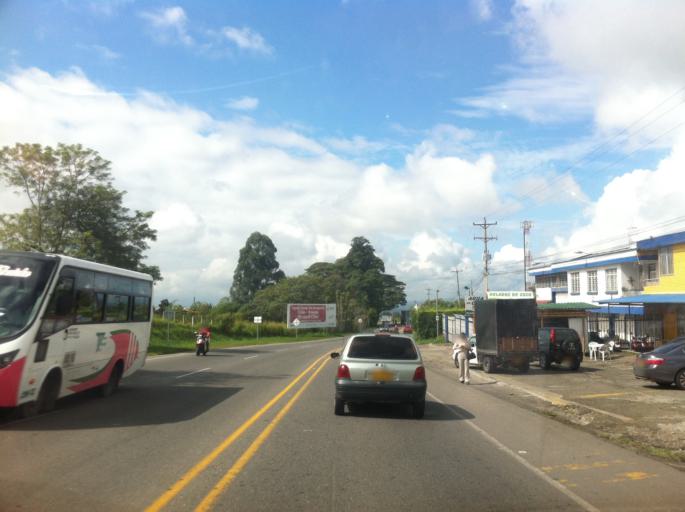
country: CO
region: Quindio
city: Armenia
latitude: 4.5099
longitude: -75.7056
